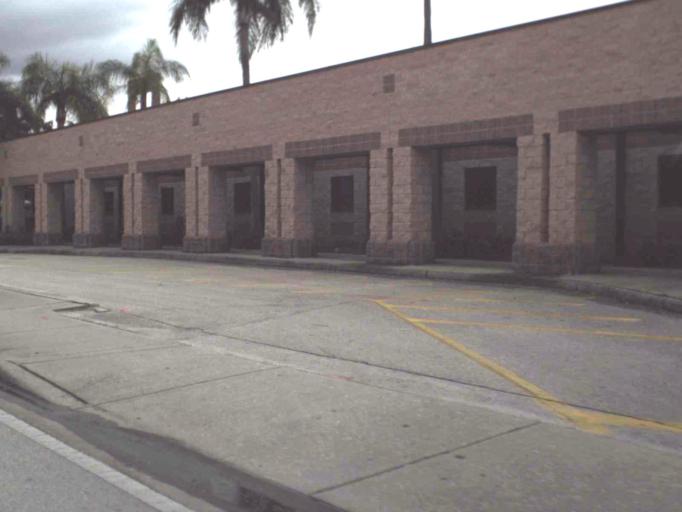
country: US
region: Florida
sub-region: Manatee County
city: Bradenton
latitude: 27.4939
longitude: -82.5600
